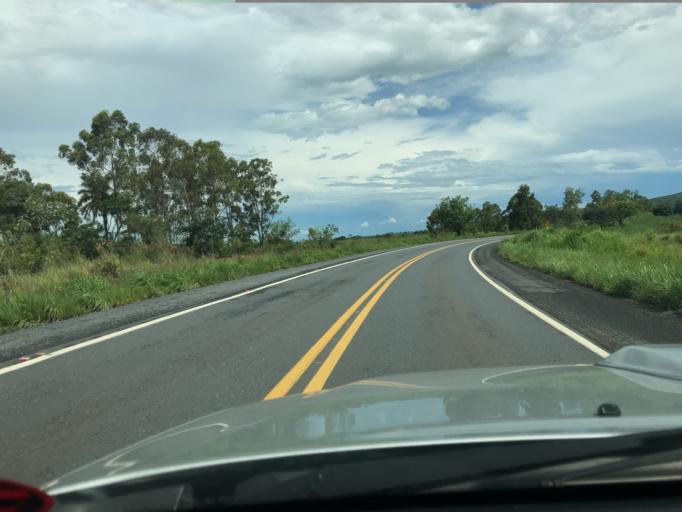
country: BR
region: Minas Gerais
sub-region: Campos Altos
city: Campos Altos
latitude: -19.8074
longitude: -46.0328
